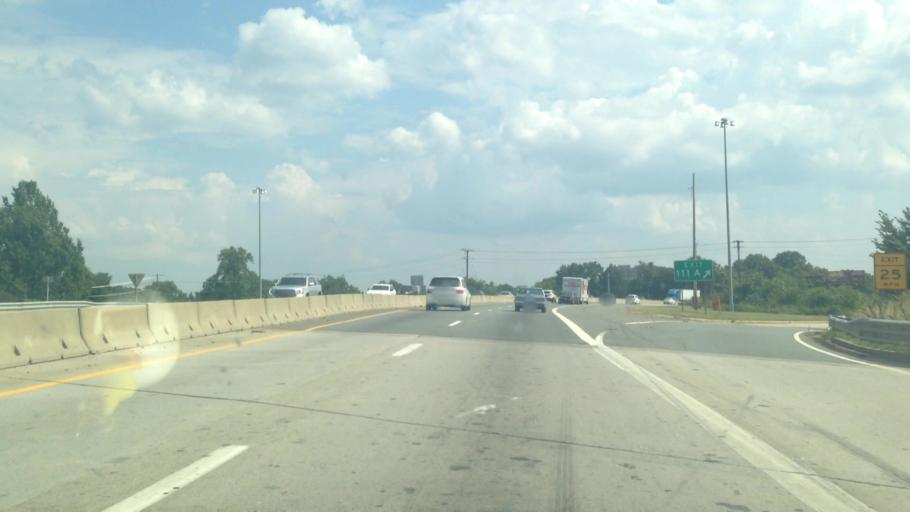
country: US
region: North Carolina
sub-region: Forsyth County
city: Winston-Salem
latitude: 36.1239
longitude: -80.2323
